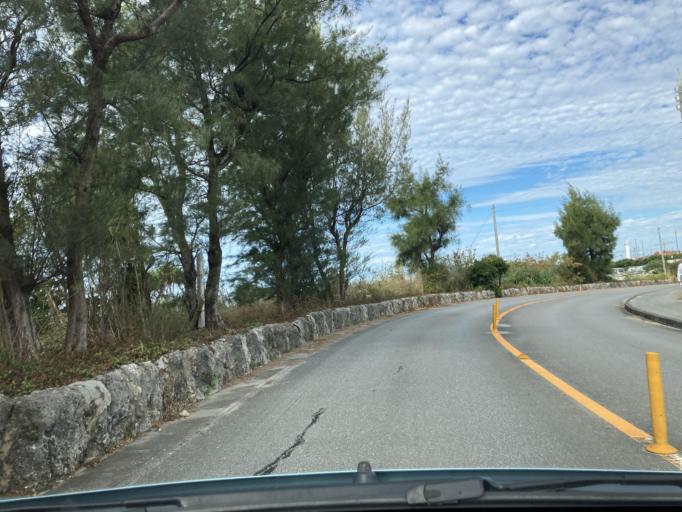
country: JP
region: Okinawa
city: Ishikawa
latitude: 26.4347
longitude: 127.7167
